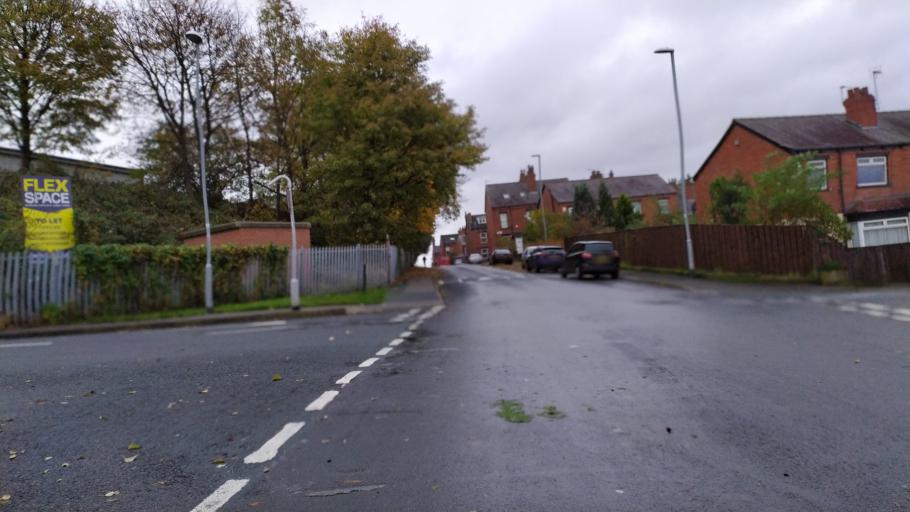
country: GB
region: England
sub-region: City and Borough of Leeds
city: Leeds
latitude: 53.8106
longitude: -1.5889
